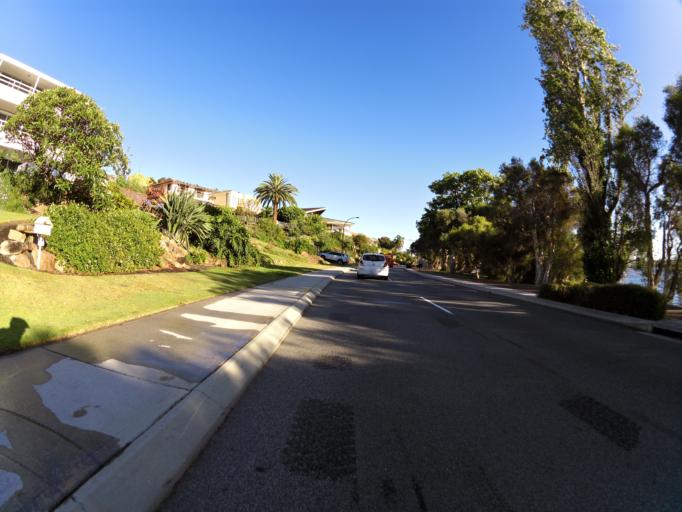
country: AU
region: Western Australia
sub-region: Melville
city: Mount Pleasant
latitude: -32.0334
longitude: 115.8534
